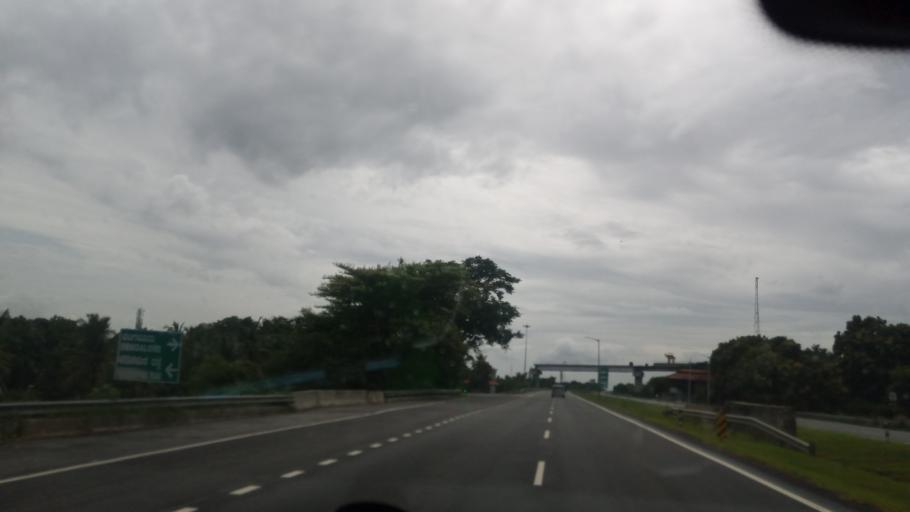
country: IN
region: Karnataka
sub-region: Bangalore Urban
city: Bangalore
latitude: 12.8563
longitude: 77.5304
